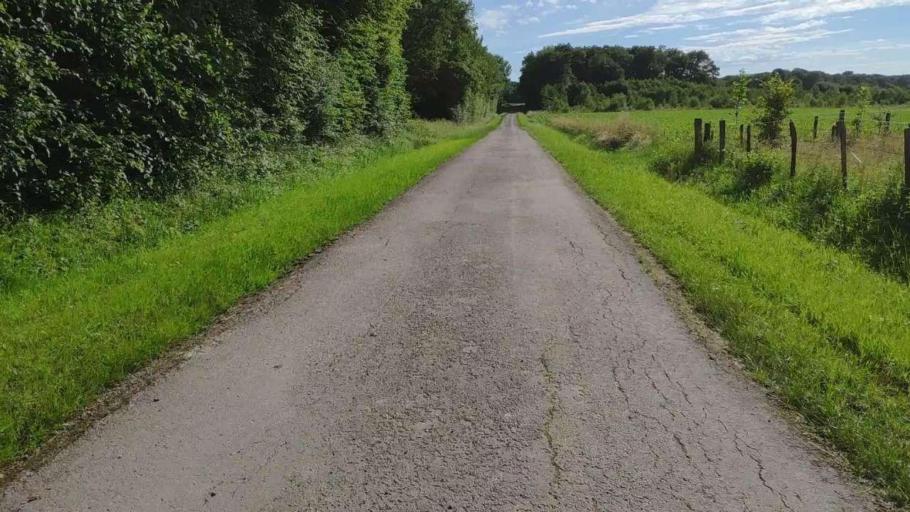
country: FR
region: Franche-Comte
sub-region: Departement du Jura
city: Bletterans
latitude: 46.8243
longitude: 5.5278
